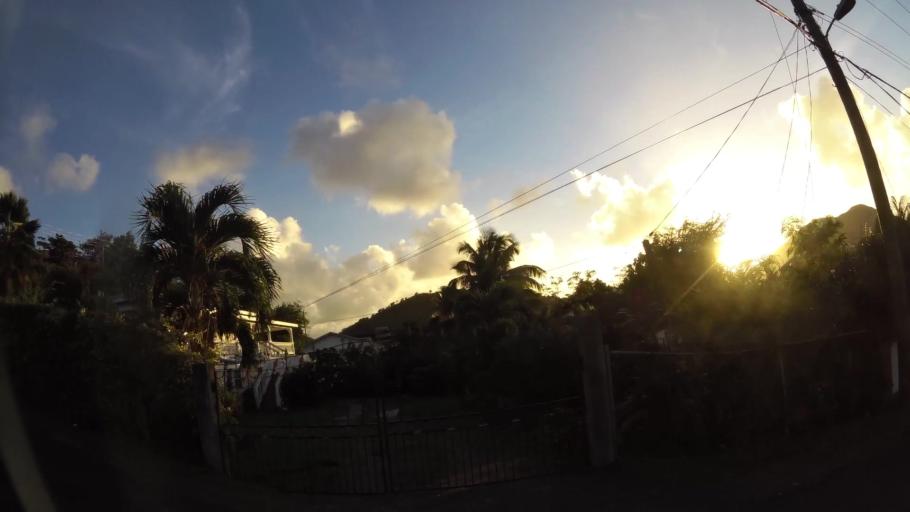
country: LC
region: Gros-Islet
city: Gros Islet
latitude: 14.0712
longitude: -60.9448
